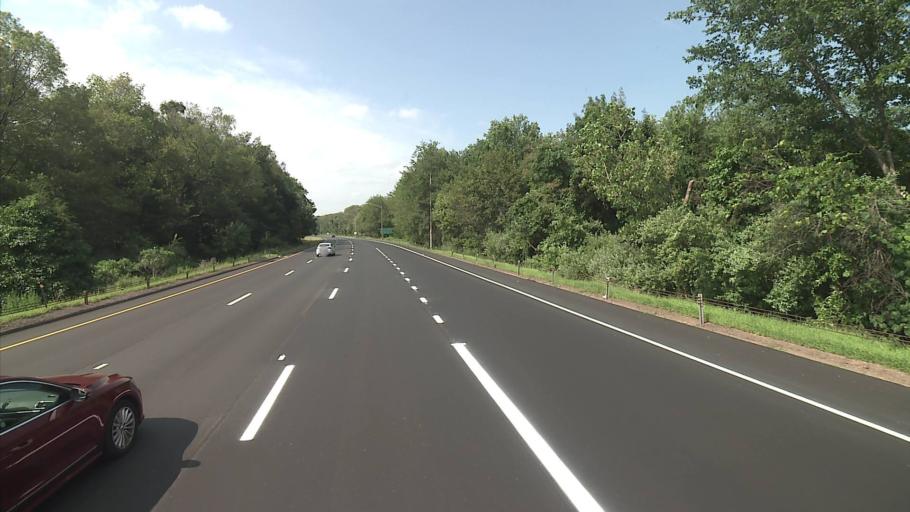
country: US
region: Connecticut
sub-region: New Haven County
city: Wallingford Center
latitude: 41.4215
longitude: -72.8265
